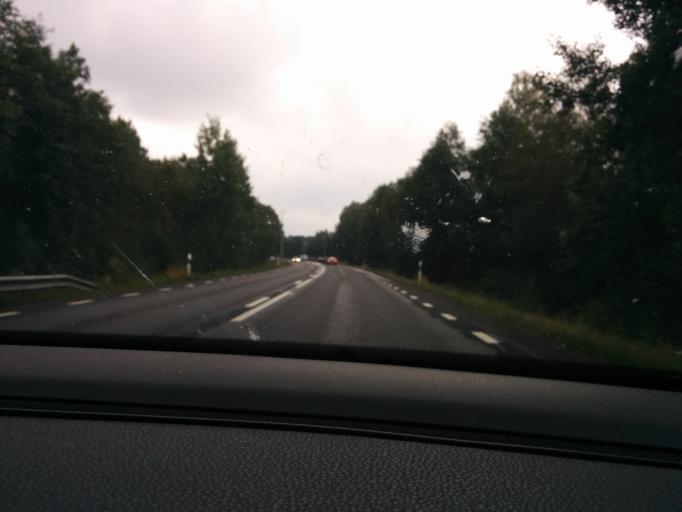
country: SE
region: Kronoberg
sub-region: Vaxjo Kommun
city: Vaexjoe
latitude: 56.8898
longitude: 14.8284
